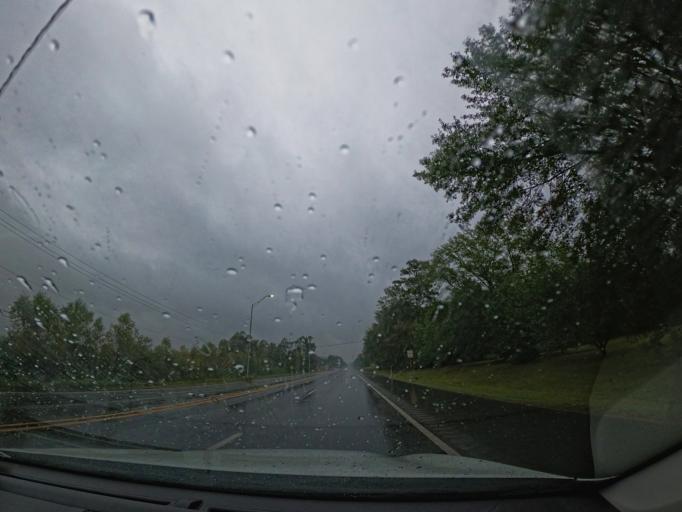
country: US
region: Texas
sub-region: Panola County
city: Carthage
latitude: 32.1597
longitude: -94.3185
